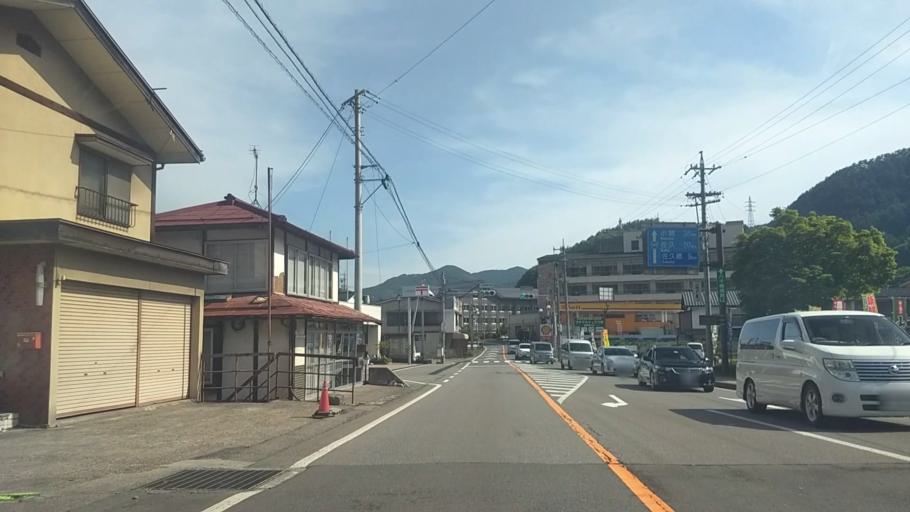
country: JP
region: Nagano
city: Saku
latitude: 36.0927
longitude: 138.4828
